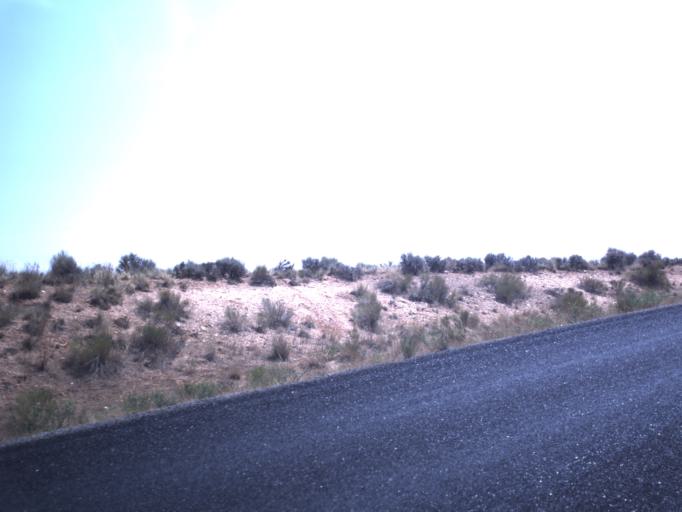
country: US
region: Utah
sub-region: Uintah County
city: Maeser
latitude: 40.4109
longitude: -109.7637
